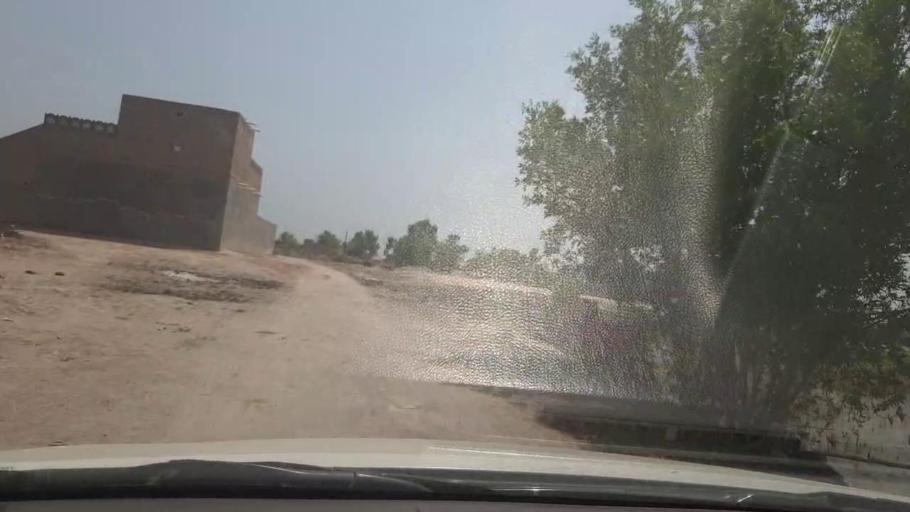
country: PK
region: Sindh
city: Shikarpur
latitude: 28.0413
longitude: 68.5733
